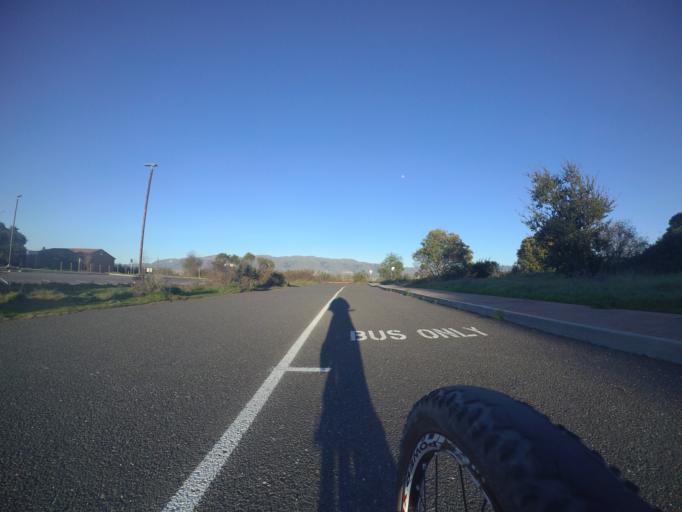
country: US
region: California
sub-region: Santa Clara County
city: Milpitas
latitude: 37.4391
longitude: -121.9594
